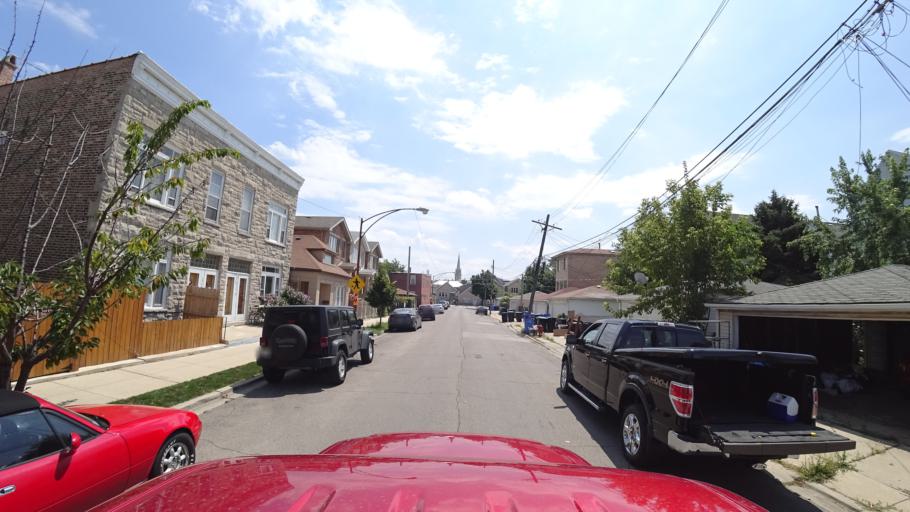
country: US
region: Illinois
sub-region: Cook County
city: Chicago
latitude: 41.8408
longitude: -87.6561
